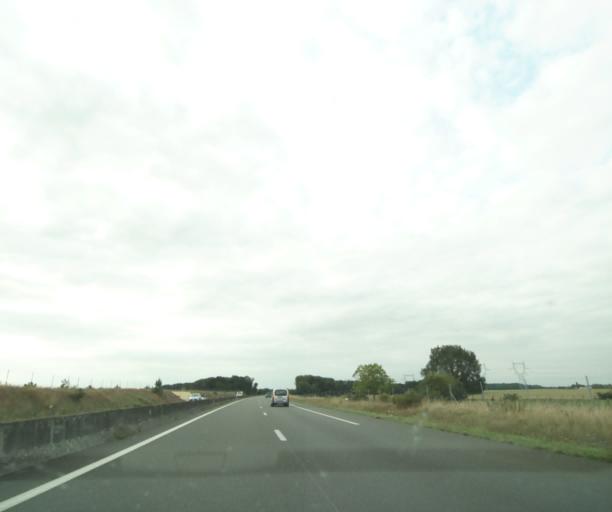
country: FR
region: Centre
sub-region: Departement d'Indre-et-Loire
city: Saint-Antoine-du-Rocher
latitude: 47.5029
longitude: 0.6417
